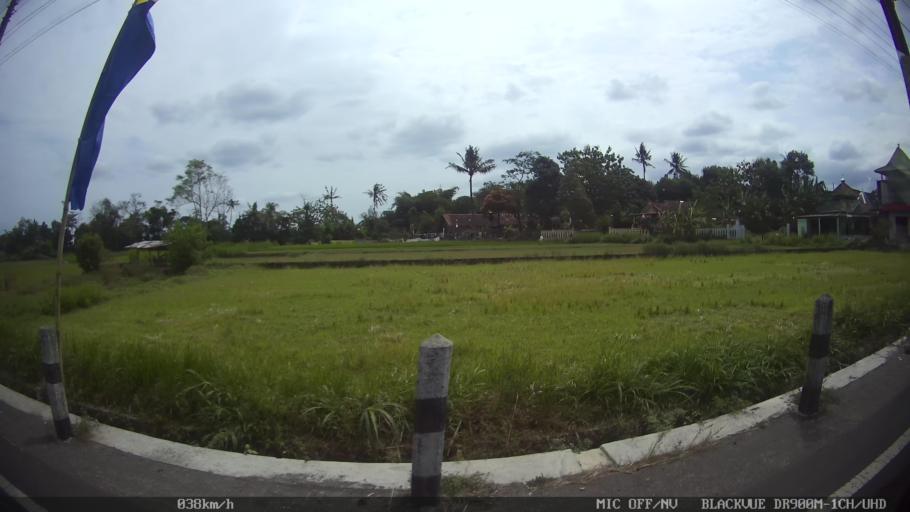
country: ID
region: Central Java
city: Candi Prambanan
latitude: -7.7393
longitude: 110.4817
